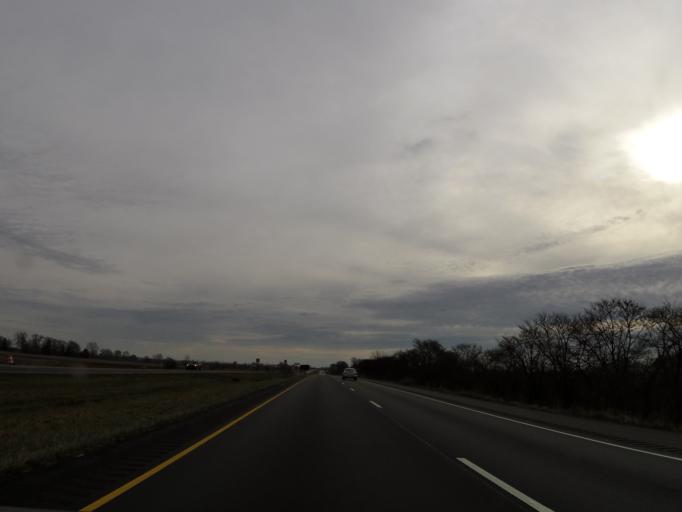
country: US
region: Indiana
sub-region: Montgomery County
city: Crawfordsville
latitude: 40.0861
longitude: -86.9299
